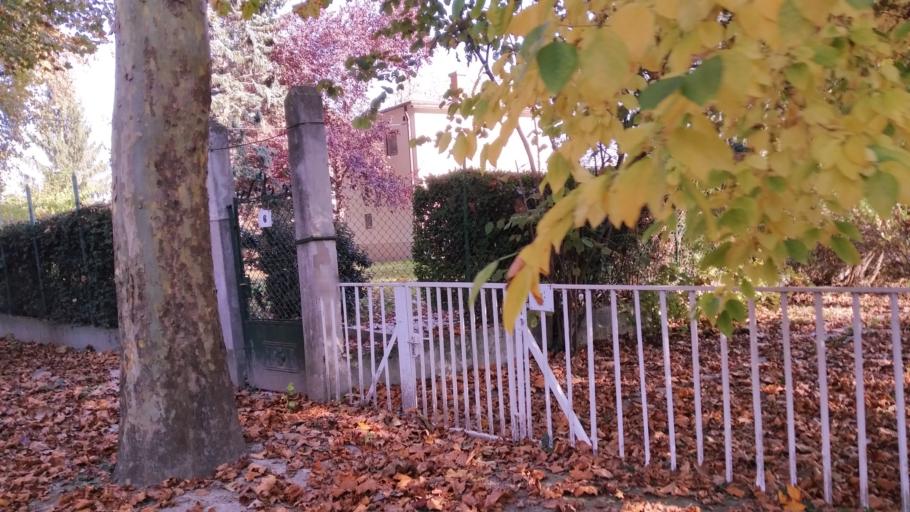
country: HU
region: Pest
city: Budakalasz
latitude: 47.6145
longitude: 19.0833
